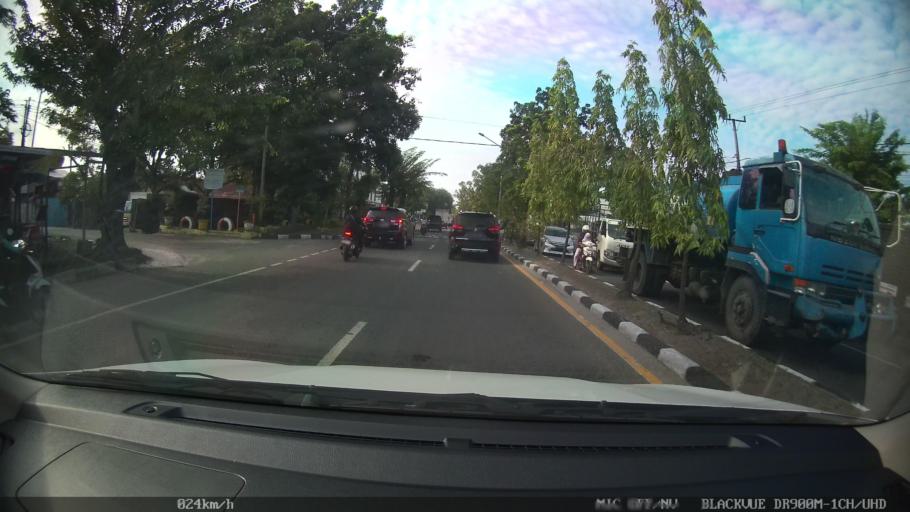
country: ID
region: North Sumatra
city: Medan
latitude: 3.6343
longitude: 98.6812
